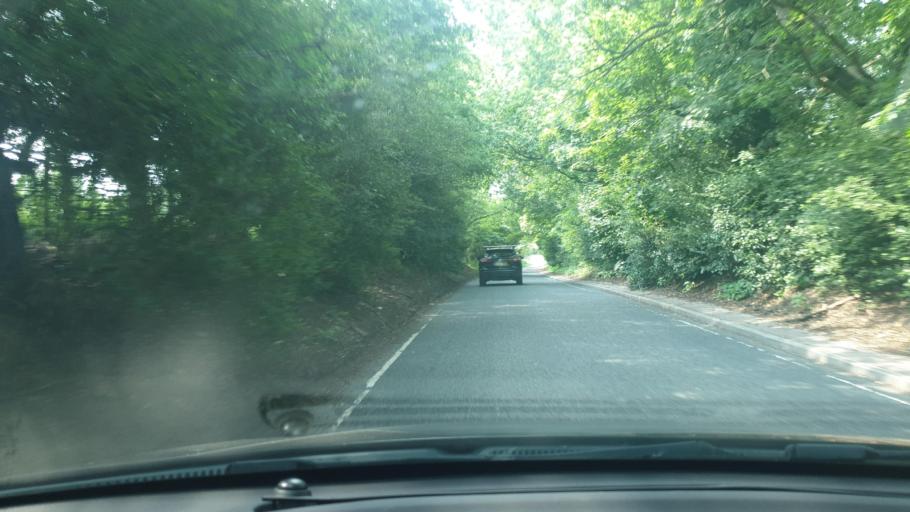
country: GB
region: England
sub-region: Suffolk
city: East Bergholt
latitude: 51.9587
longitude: 0.9766
